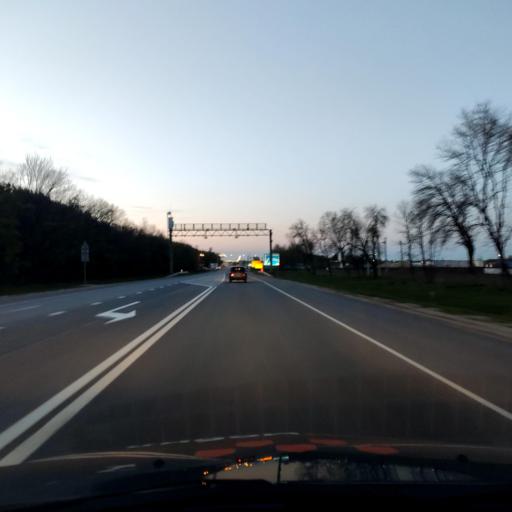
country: RU
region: Orjol
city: Zmiyevka
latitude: 52.7060
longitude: 36.3636
